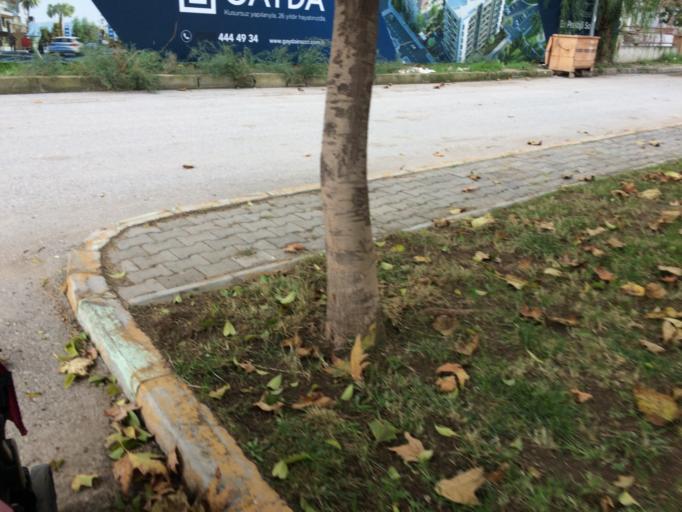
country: TR
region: Izmir
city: Karsiyaka
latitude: 38.4845
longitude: 27.0601
